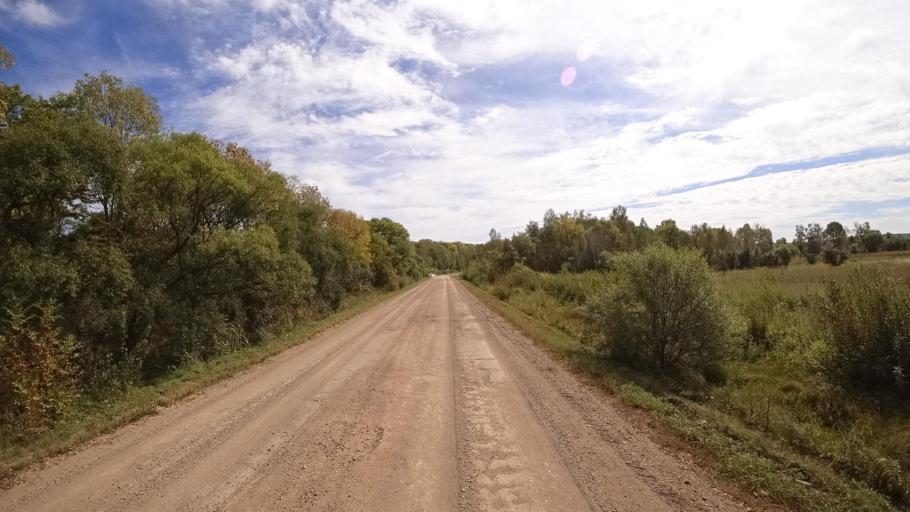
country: RU
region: Primorskiy
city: Yakovlevka
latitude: 44.6359
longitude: 133.5984
